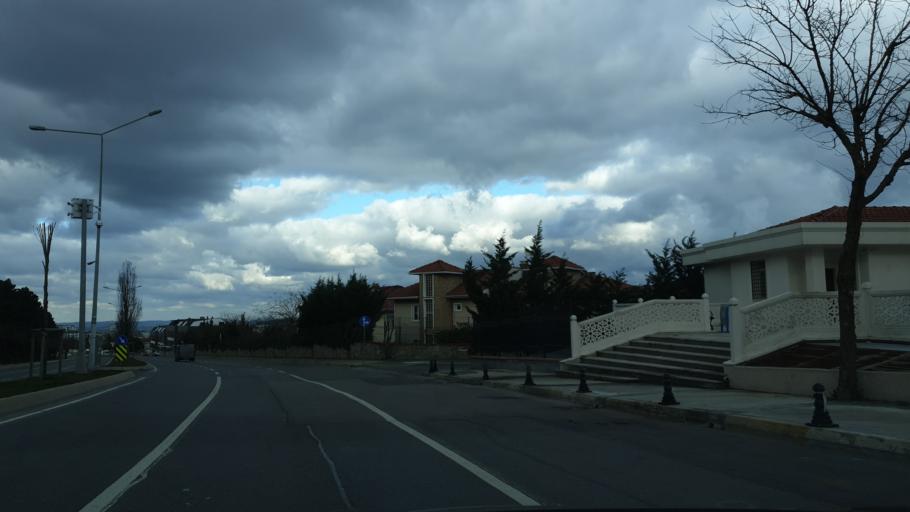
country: TR
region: Istanbul
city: Sultanbeyli
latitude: 40.9252
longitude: 29.2691
